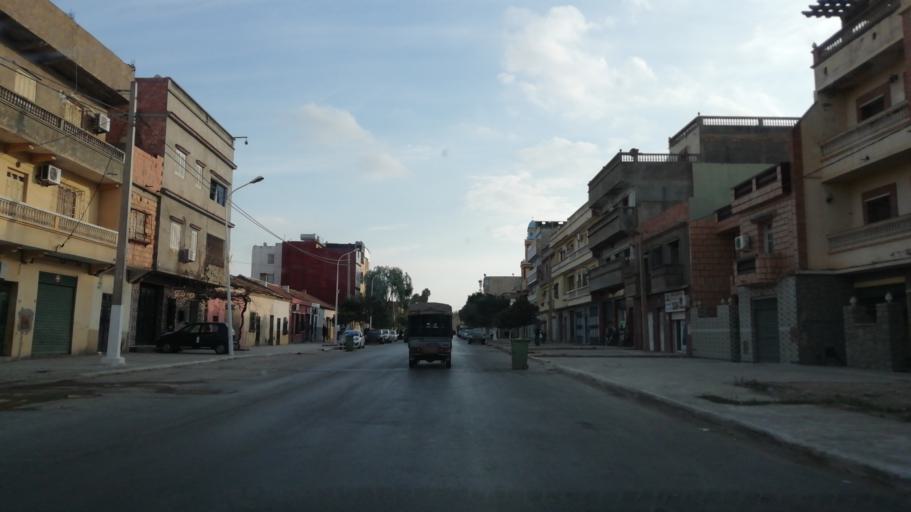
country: DZ
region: Mascara
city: Mascara
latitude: 35.5967
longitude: 0.0642
